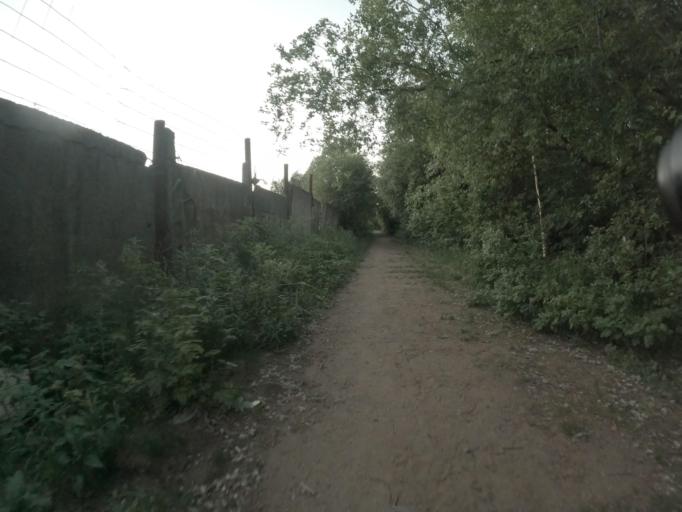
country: RU
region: St.-Petersburg
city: Krasnogvargeisky
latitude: 59.9888
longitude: 30.5319
